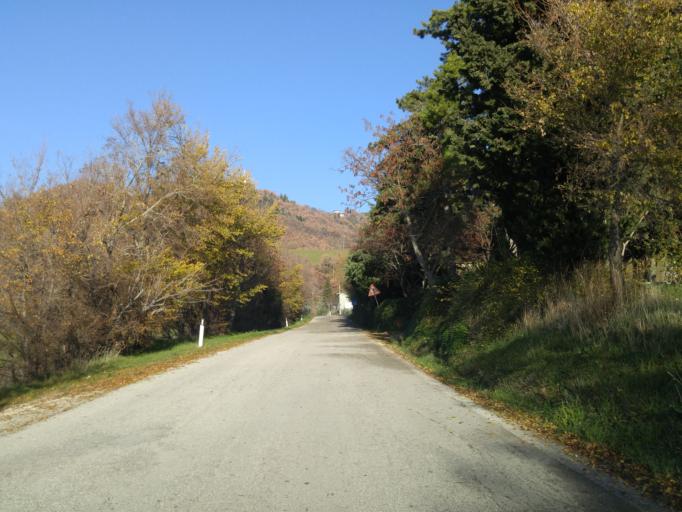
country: IT
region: The Marches
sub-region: Provincia di Pesaro e Urbino
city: Isola del Piano
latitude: 43.7647
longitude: 12.7995
